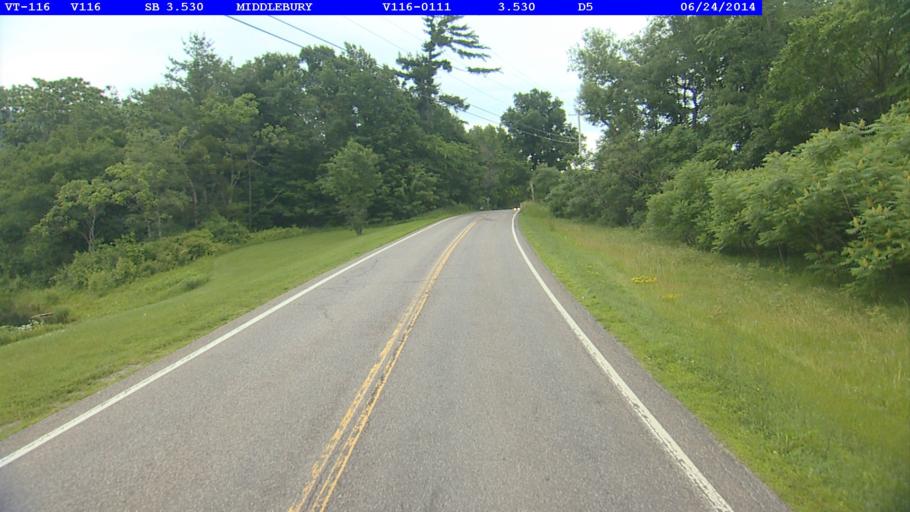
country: US
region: Vermont
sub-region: Addison County
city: Middlebury (village)
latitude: 44.0136
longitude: -73.1003
